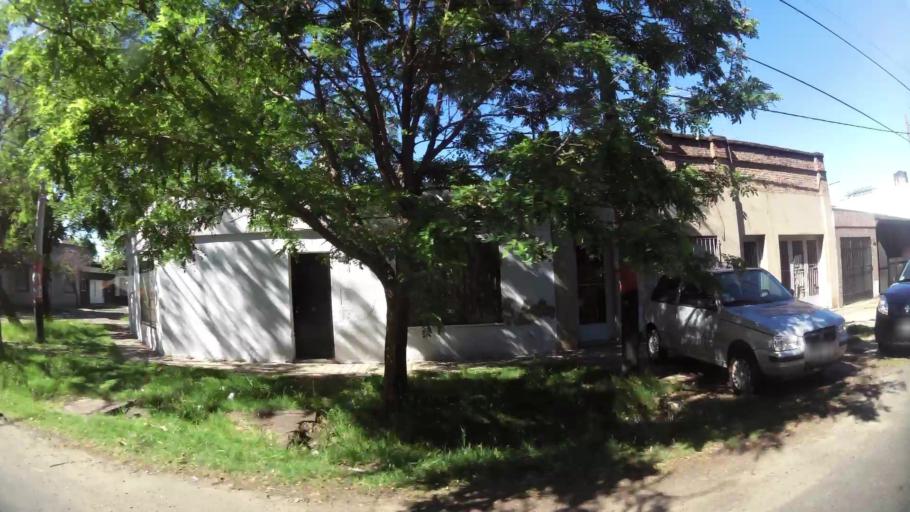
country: AR
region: Santa Fe
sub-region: Departamento de Rosario
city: Rosario
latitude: -32.9566
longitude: -60.6851
